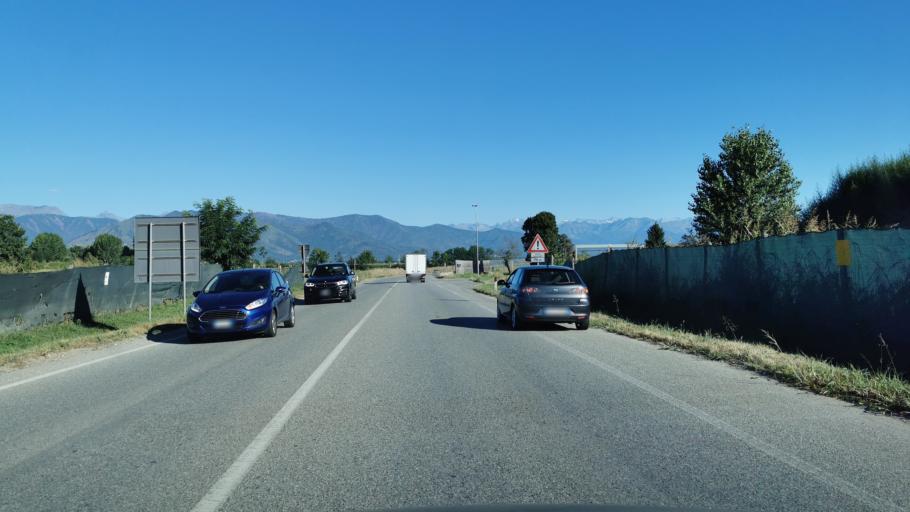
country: IT
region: Piedmont
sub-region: Provincia di Torino
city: Savonera
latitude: 45.1096
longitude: 7.5940
